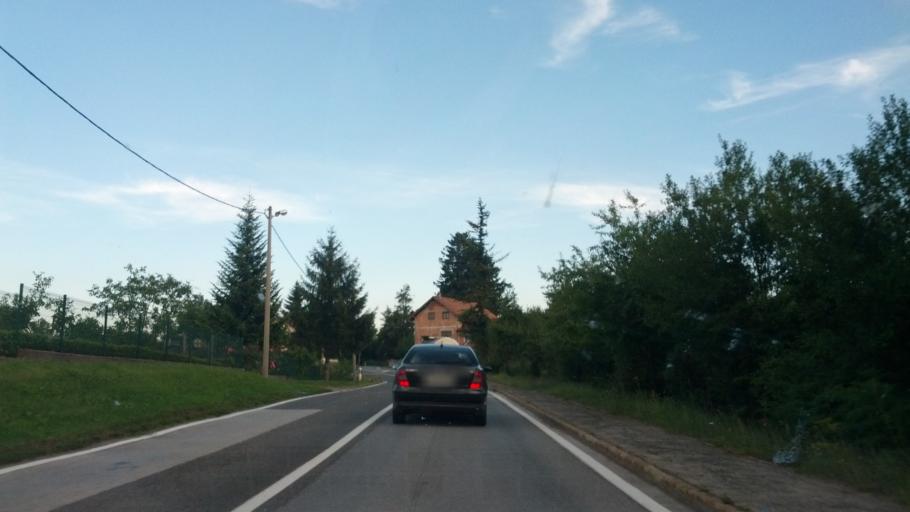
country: HR
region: Licko-Senjska
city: Jezerce
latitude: 44.9517
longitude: 15.6730
